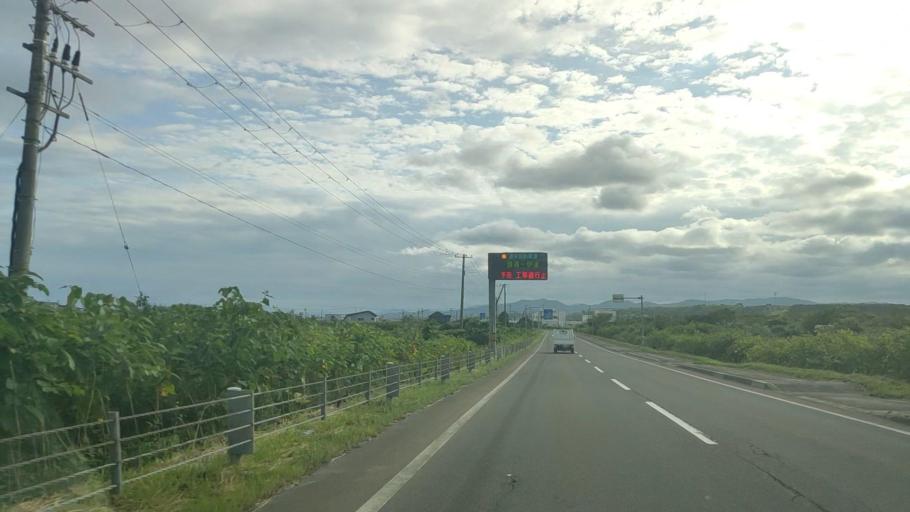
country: JP
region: Hokkaido
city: Niseko Town
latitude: 42.5233
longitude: 140.3871
